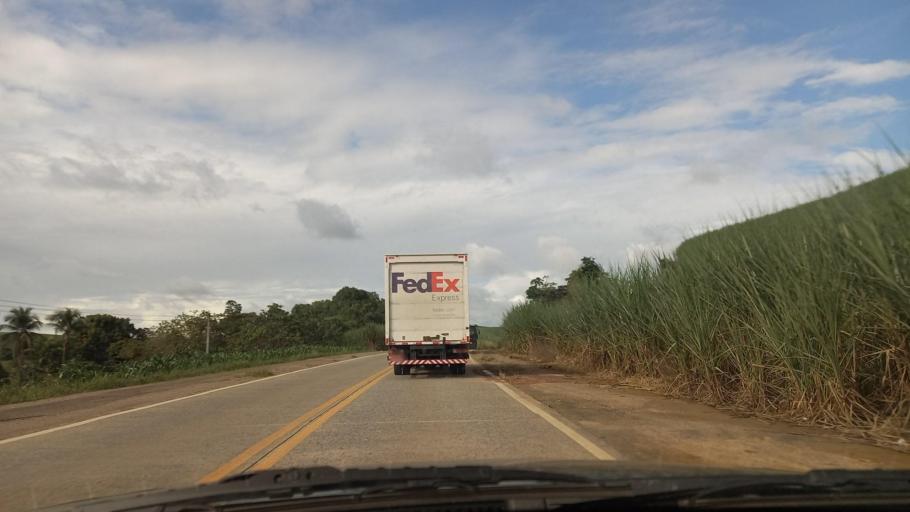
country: BR
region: Pernambuco
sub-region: Palmares
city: Palmares
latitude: -8.6949
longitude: -35.6565
